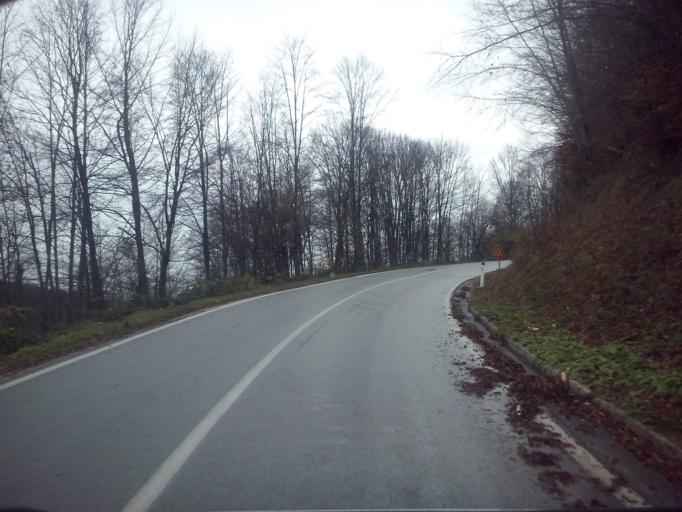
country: RS
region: Central Serbia
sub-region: Moravicki Okrug
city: Ivanjica
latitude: 43.5256
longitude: 20.3296
